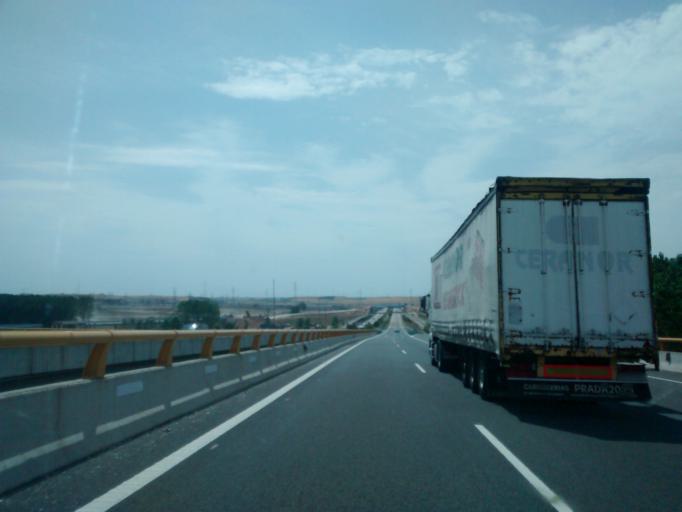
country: ES
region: Castille and Leon
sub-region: Provincia de Burgos
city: San Mames de Burgos
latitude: 42.3528
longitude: -3.7969
